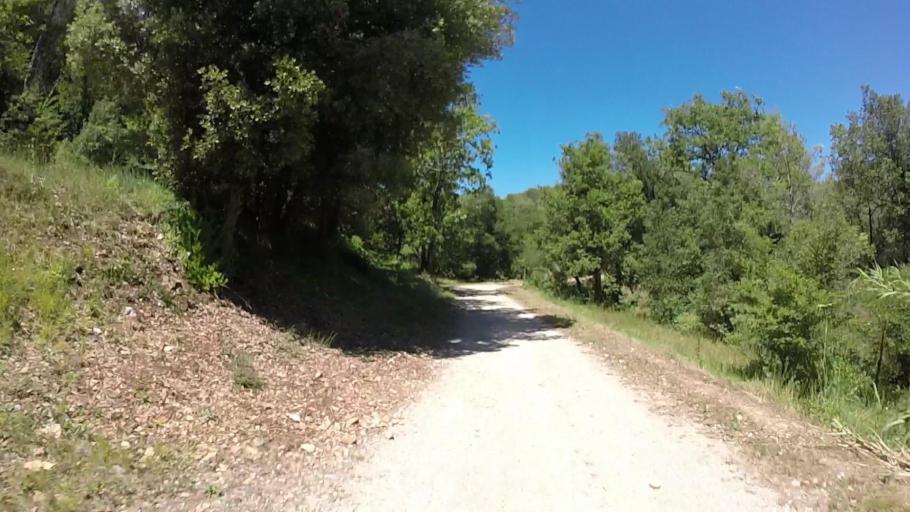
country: FR
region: Provence-Alpes-Cote d'Azur
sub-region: Departement des Alpes-Maritimes
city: Valbonne
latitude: 43.6307
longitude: 7.0258
